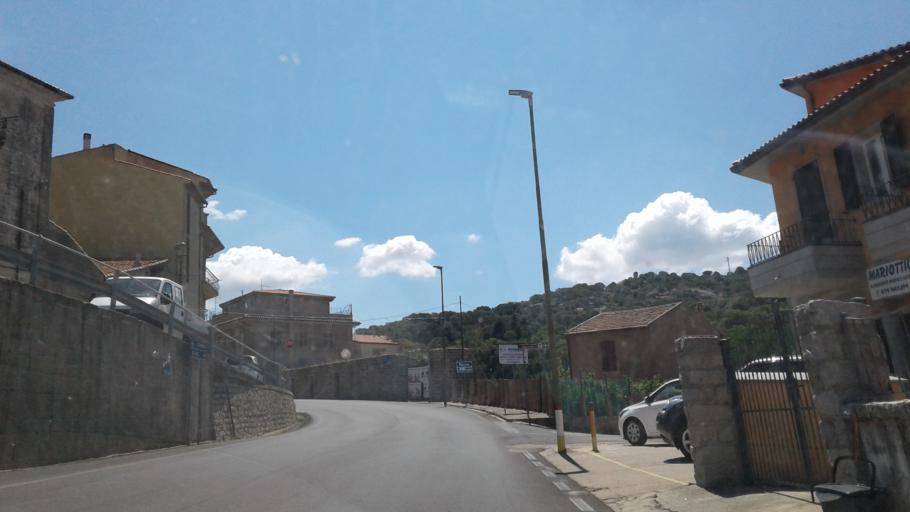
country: IT
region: Sardinia
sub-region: Provincia di Olbia-Tempio
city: Calangianus
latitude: 40.9211
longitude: 9.1897
